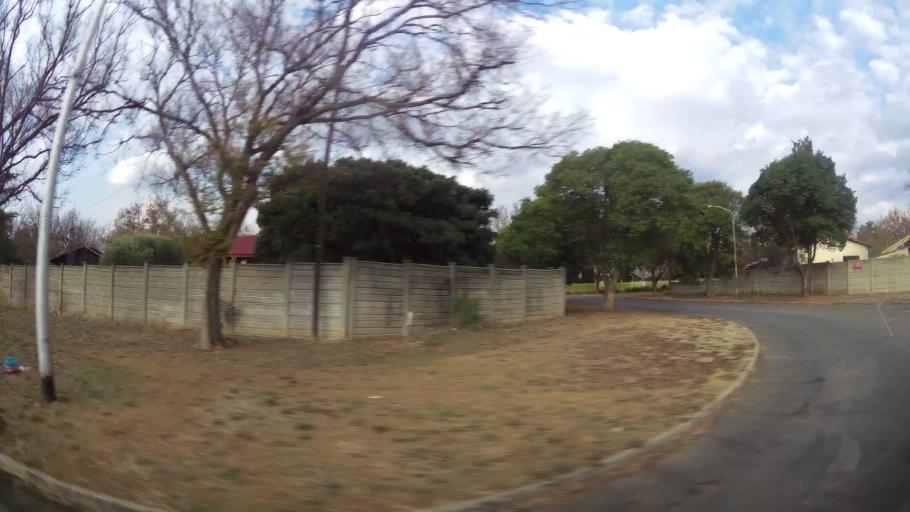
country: ZA
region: Orange Free State
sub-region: Fezile Dabi District Municipality
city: Sasolburg
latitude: -26.8109
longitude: 27.8096
